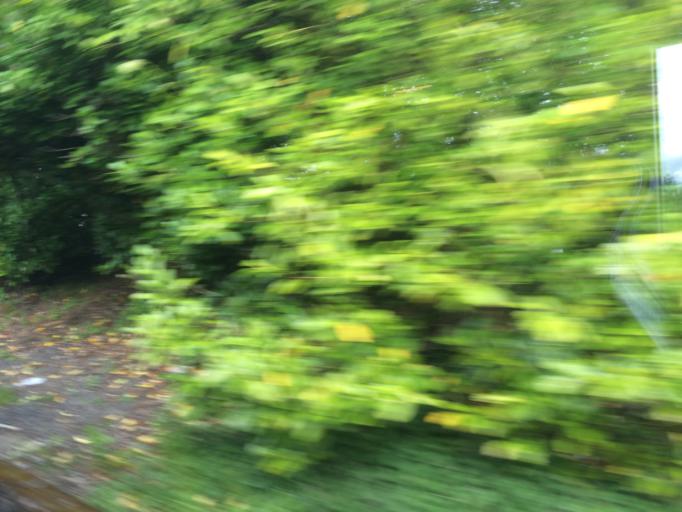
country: GB
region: Scotland
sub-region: Perth and Kinross
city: Auchterarder
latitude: 56.2743
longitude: -3.7310
